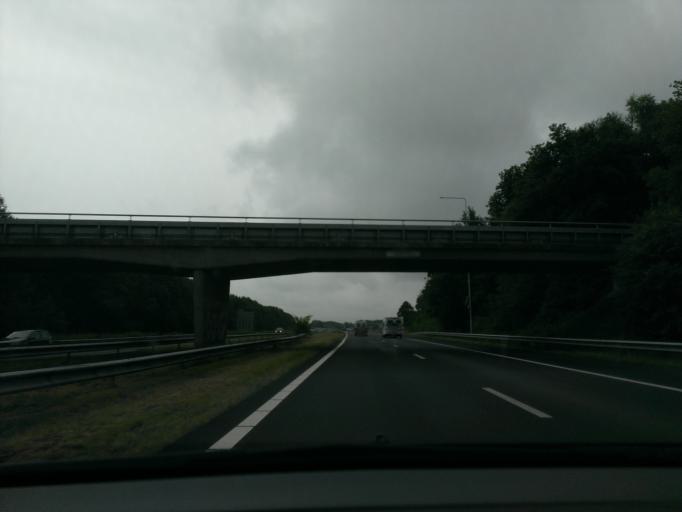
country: NL
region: Drenthe
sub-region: Gemeente Westerveld
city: Dwingeloo
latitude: 52.8678
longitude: 6.5028
